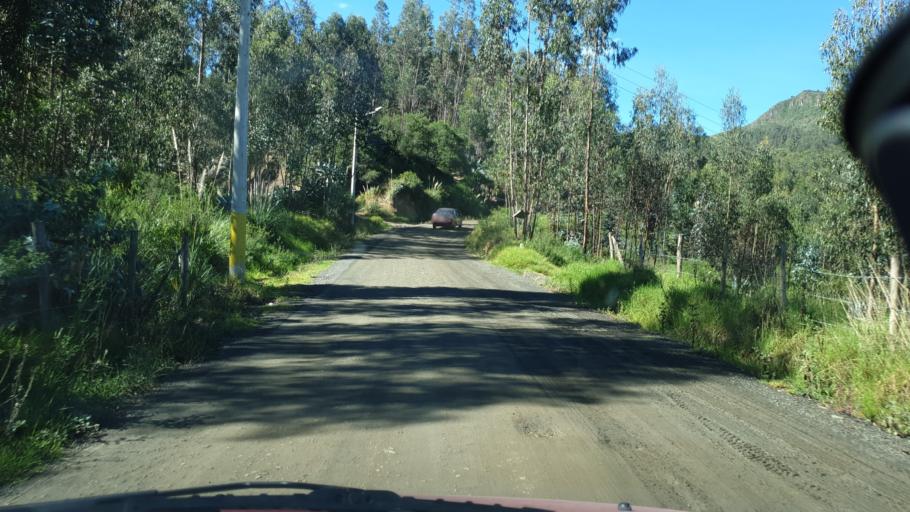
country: EC
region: Azuay
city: Llacao
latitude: -2.8731
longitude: -78.9076
